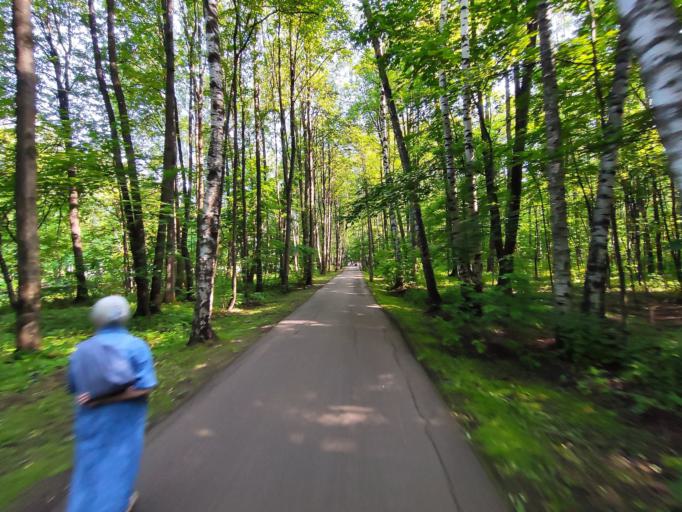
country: RU
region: Moscow
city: Metrogorodok
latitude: 55.7832
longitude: 37.7528
